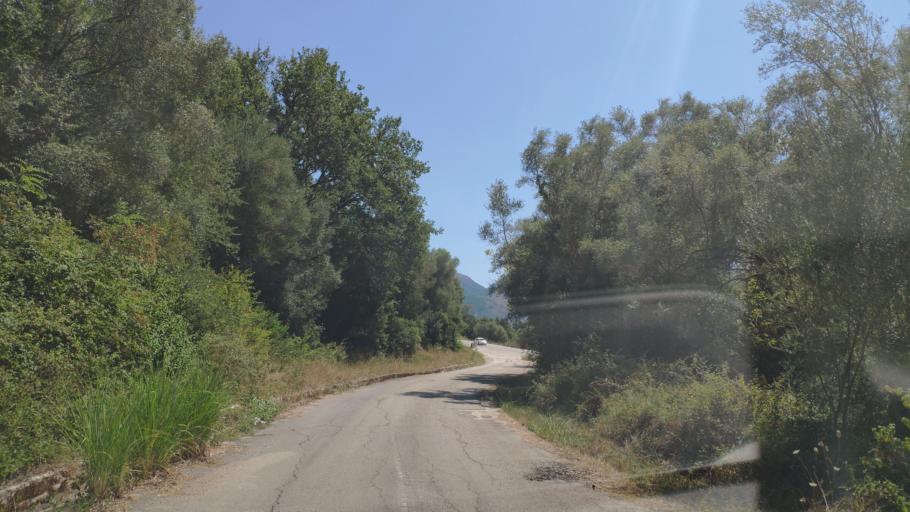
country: GR
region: Epirus
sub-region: Nomos Prevezis
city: Kanalaki
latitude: 39.2686
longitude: 20.6007
